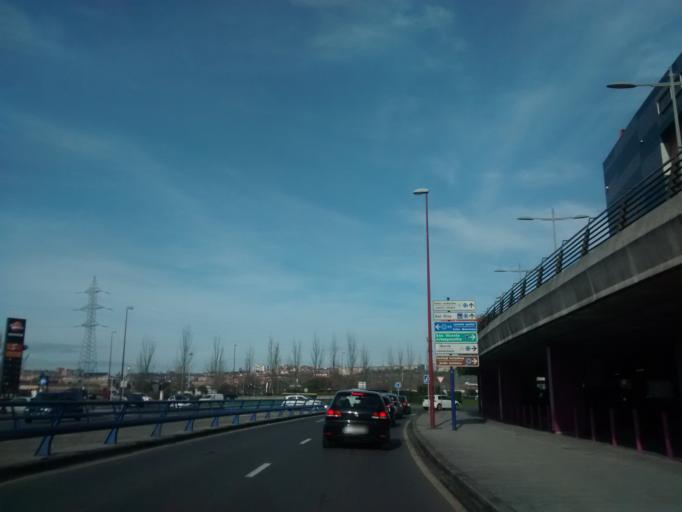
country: ES
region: Basque Country
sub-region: Bizkaia
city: Barakaldo
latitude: 43.2929
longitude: -3.0058
